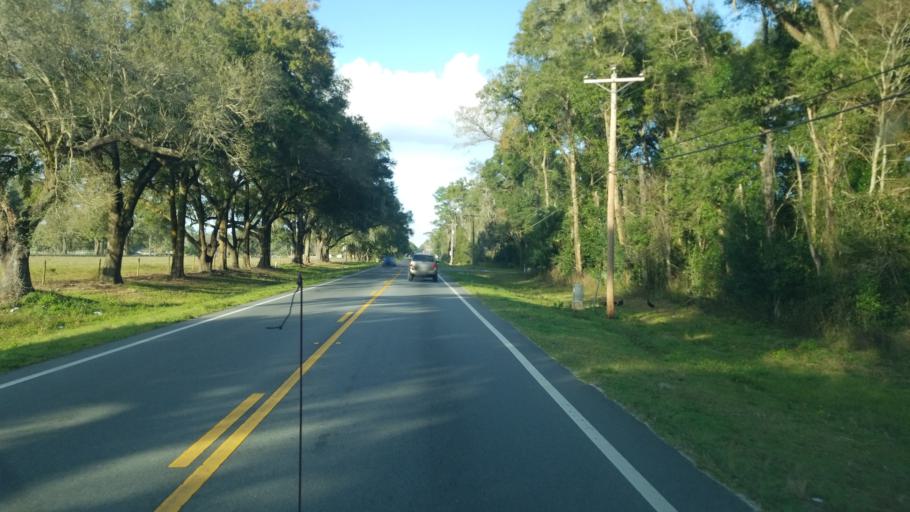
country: US
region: Florida
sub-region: Marion County
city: Ocala
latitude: 29.2252
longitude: -82.1233
